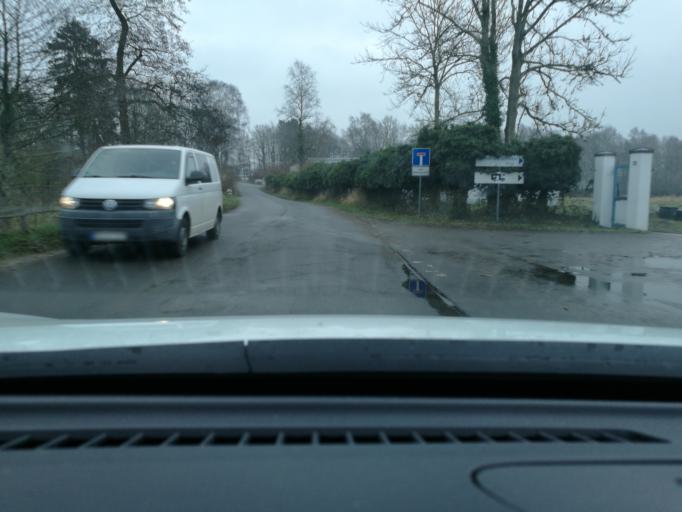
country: DE
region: Schleswig-Holstein
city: Borgstedt
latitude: 54.3303
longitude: 9.7160
